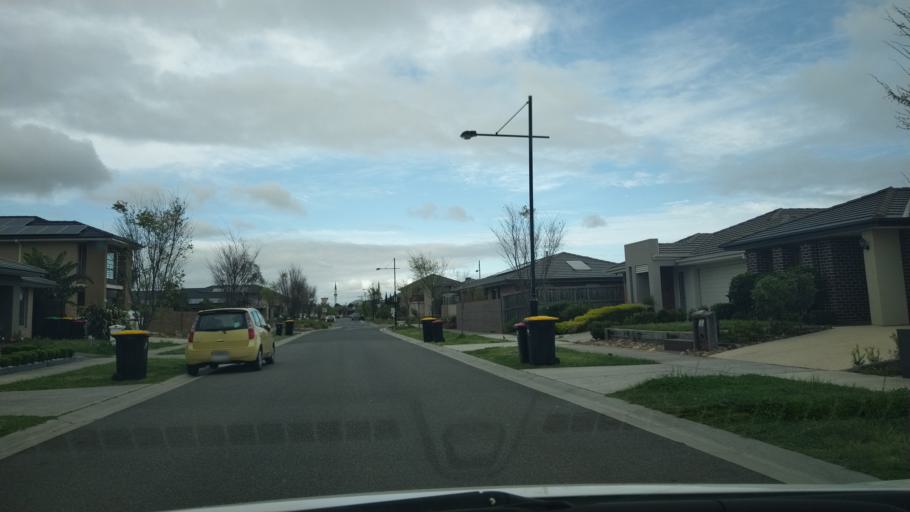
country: AU
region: Victoria
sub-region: Greater Dandenong
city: Keysborough
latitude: -38.0071
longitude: 145.1788
